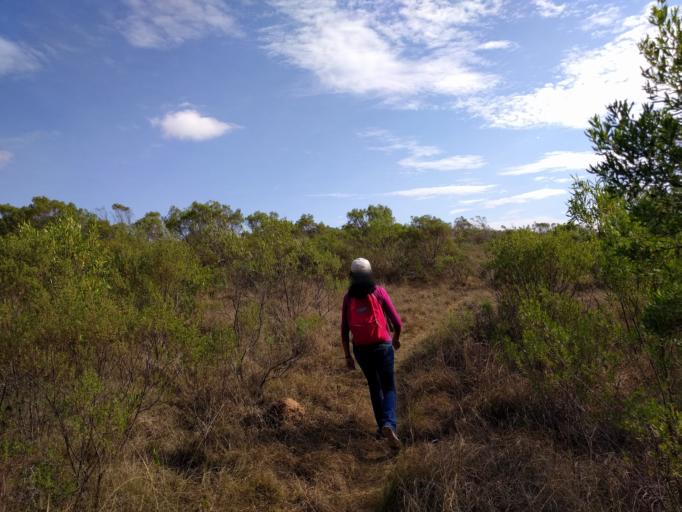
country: BO
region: Santa Cruz
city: Samaipata
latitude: -18.1857
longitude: -63.8908
